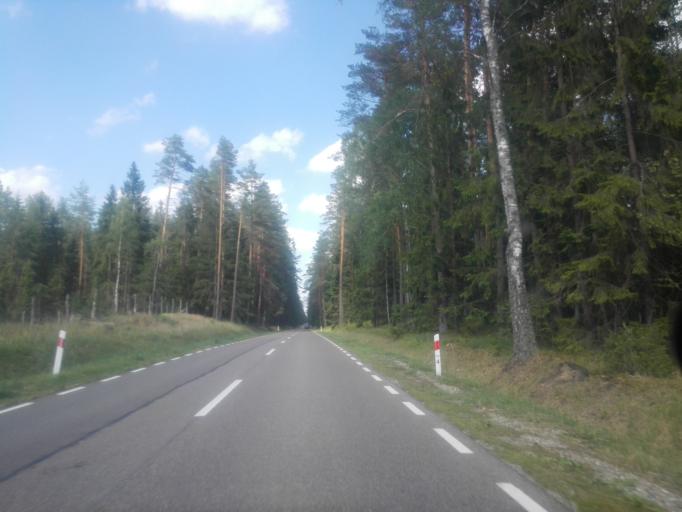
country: PL
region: Podlasie
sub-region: Powiat augustowski
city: Augustow
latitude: 53.9109
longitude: 23.1410
